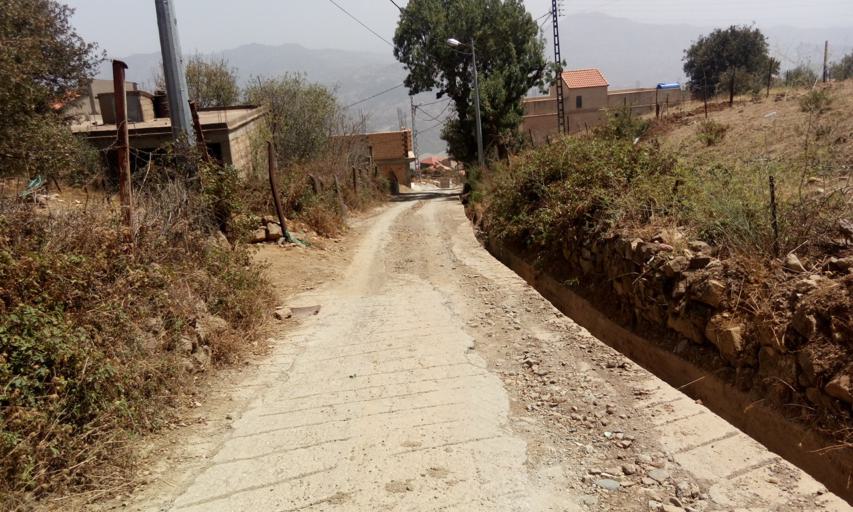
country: DZ
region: Tizi Ouzou
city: Chemini
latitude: 36.6095
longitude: 4.6319
